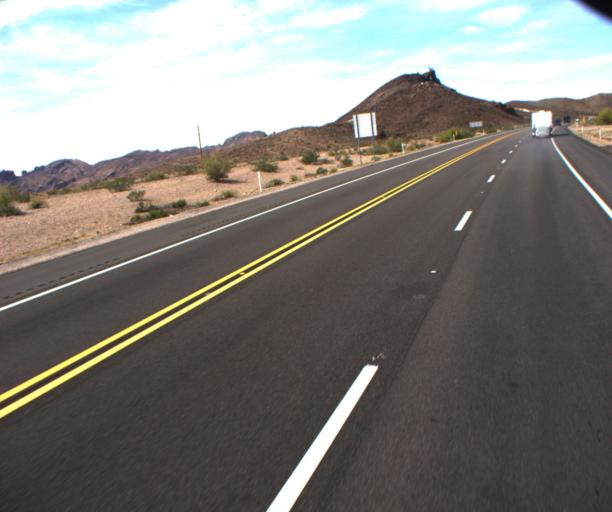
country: US
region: Arizona
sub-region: Mohave County
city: Desert Hills
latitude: 34.5913
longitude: -114.3697
